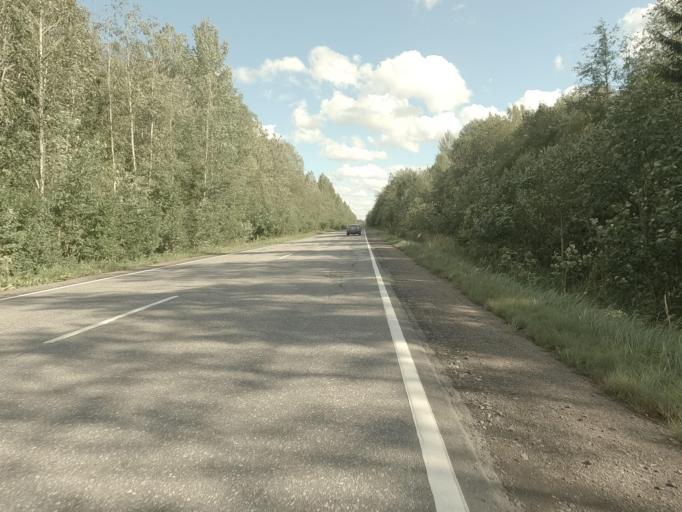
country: RU
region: Leningrad
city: Shcheglovo
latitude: 59.9956
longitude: 30.8772
